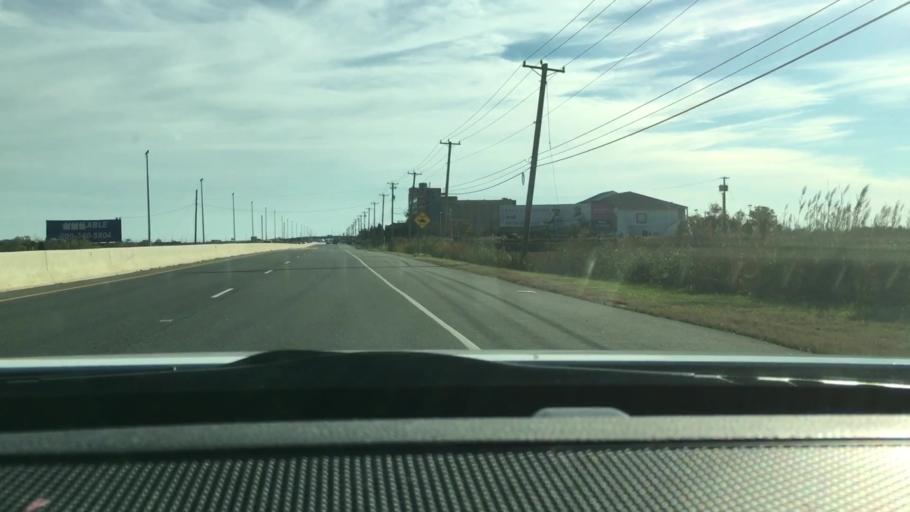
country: US
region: New Jersey
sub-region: Atlantic County
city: Absecon
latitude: 39.4074
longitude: -74.4919
